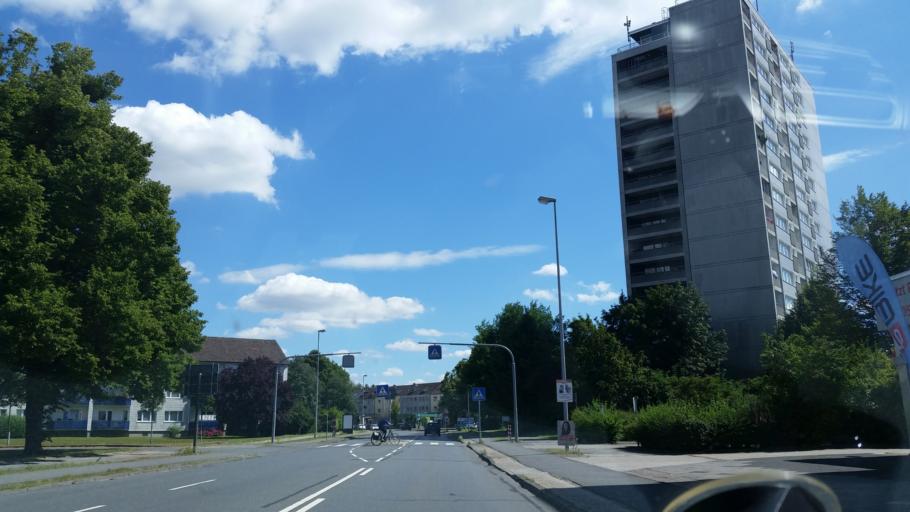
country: DE
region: Lower Saxony
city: Wolfsburg
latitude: 52.4259
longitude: 10.7697
